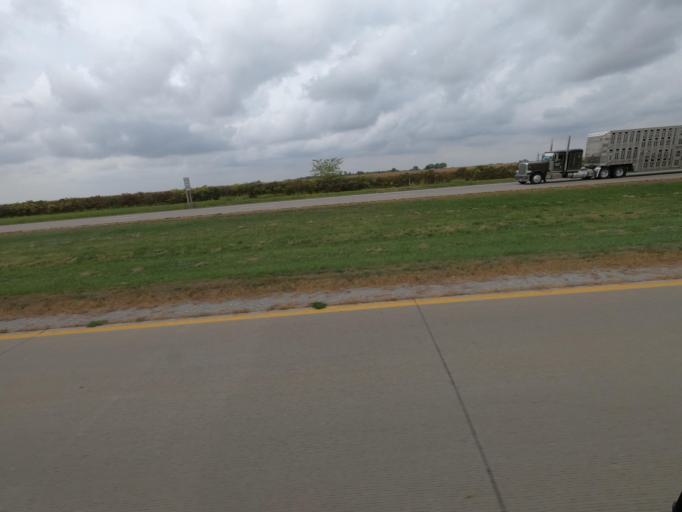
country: US
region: Iowa
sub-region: Wapello County
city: Ottumwa
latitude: 41.0020
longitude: -92.2508
